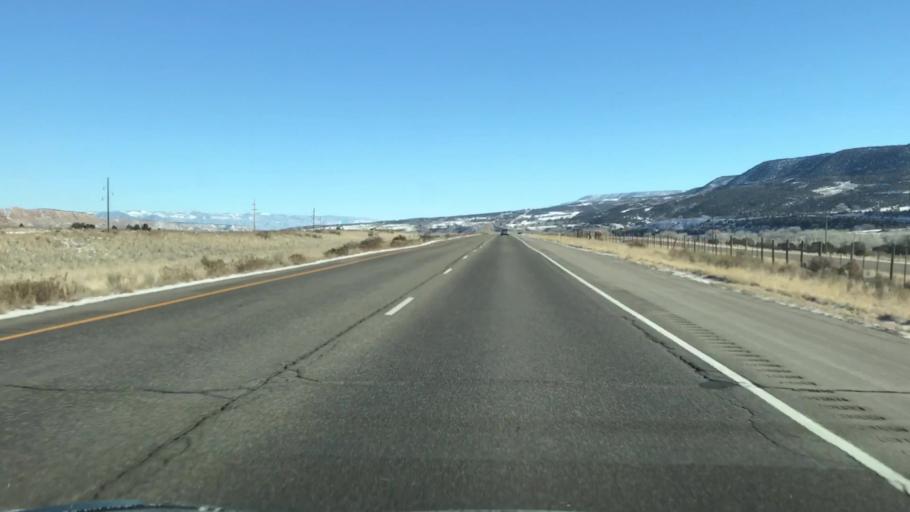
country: US
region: Colorado
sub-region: Garfield County
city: Battlement Mesa
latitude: 39.4775
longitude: -107.9818
